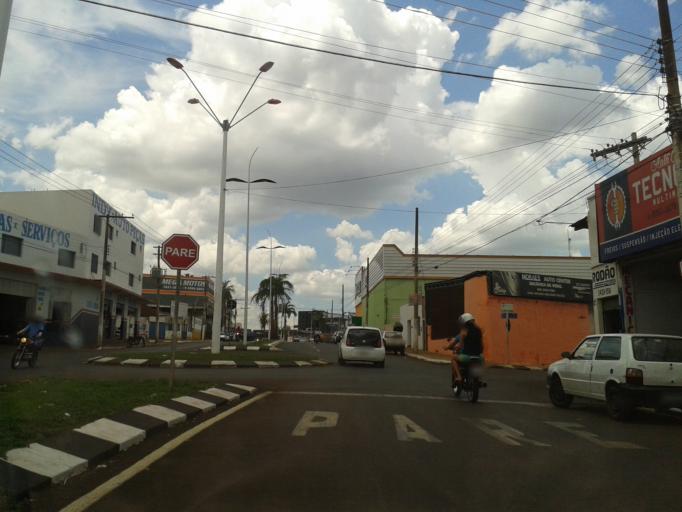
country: BR
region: Goias
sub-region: Itumbiara
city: Itumbiara
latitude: -18.4069
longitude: -49.2112
